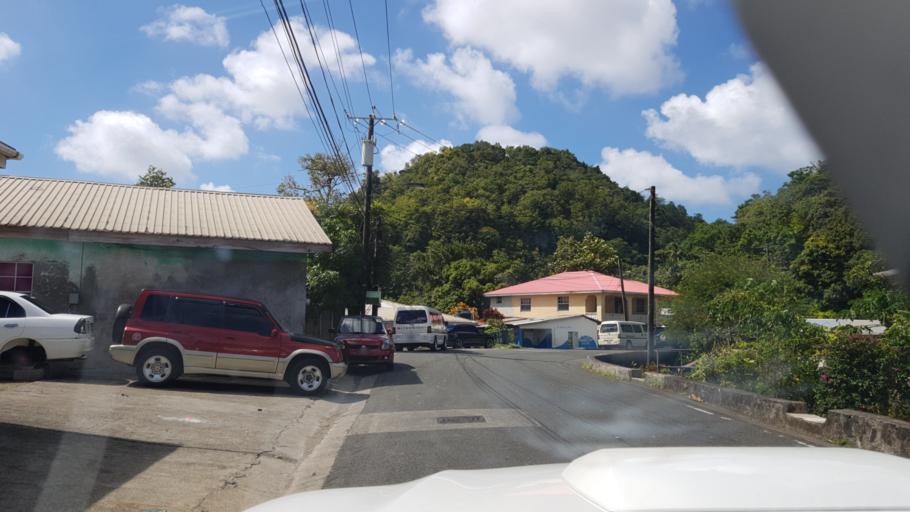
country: LC
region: Castries Quarter
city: Castries
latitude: 13.9885
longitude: -60.9722
